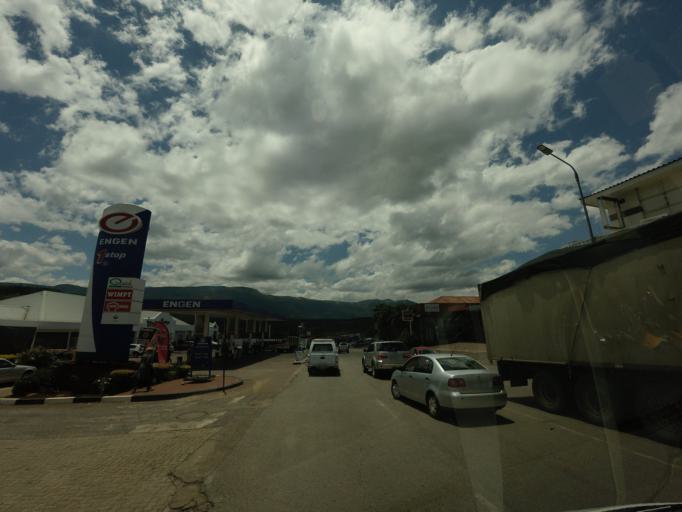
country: ZA
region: Mpumalanga
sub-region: Ehlanzeni District
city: Graksop
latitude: -25.0977
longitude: 30.7789
